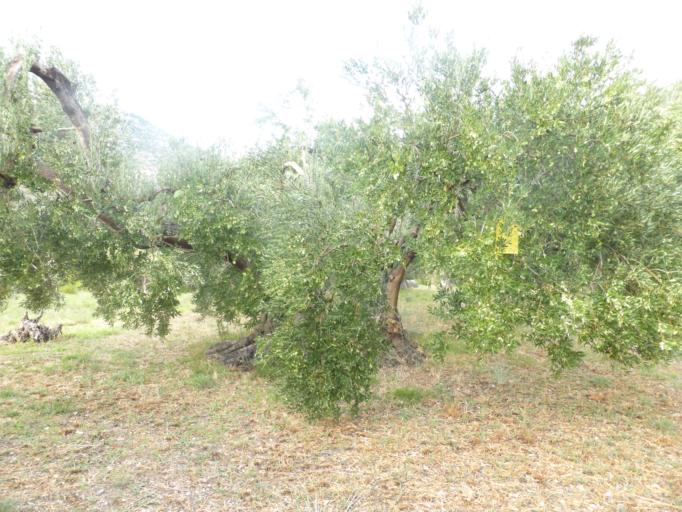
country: HR
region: Dubrovacko-Neretvanska
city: Podgora
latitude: 42.7904
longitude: 17.8841
